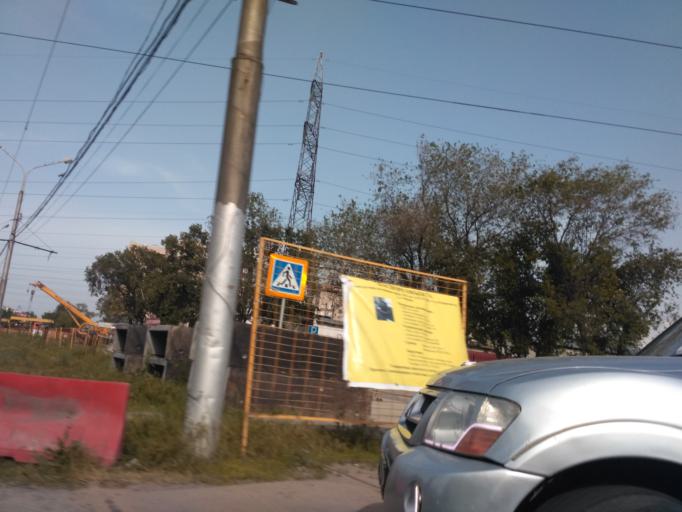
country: KZ
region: Almaty Qalasy
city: Almaty
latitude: 43.2437
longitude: 76.8494
